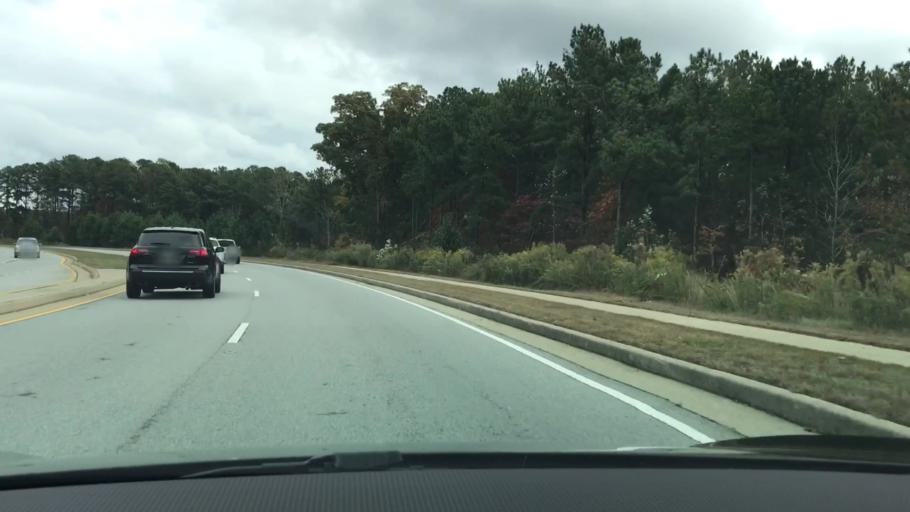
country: US
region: Georgia
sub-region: Gwinnett County
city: Suwanee
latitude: 34.0209
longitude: -84.0471
